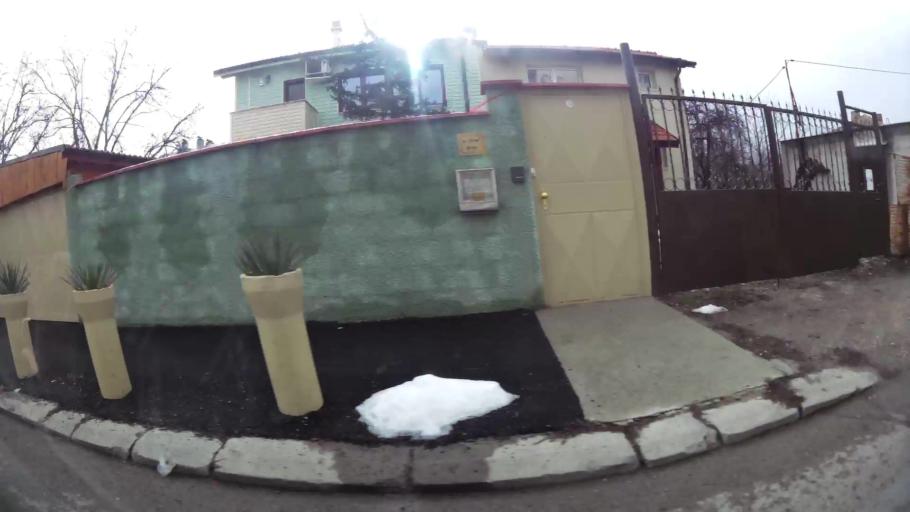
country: BG
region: Sofia-Capital
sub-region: Stolichna Obshtina
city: Sofia
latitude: 42.7444
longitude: 23.2711
